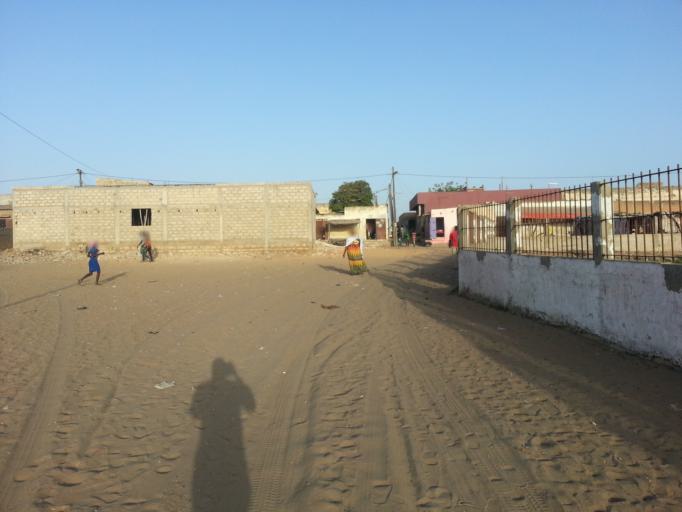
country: SN
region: Dakar
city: Pikine
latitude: 14.7722
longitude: -17.3826
